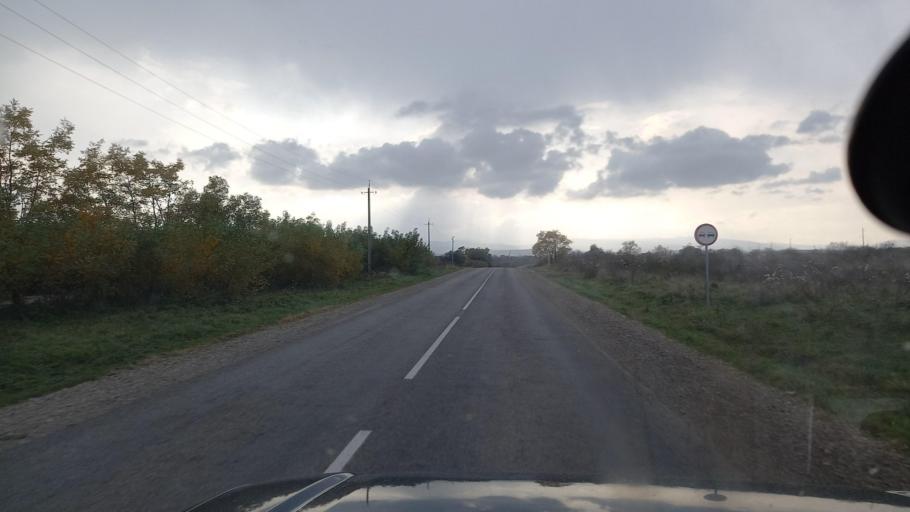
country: RU
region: Krasnodarskiy
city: Gubskaya
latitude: 44.3531
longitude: 40.6990
